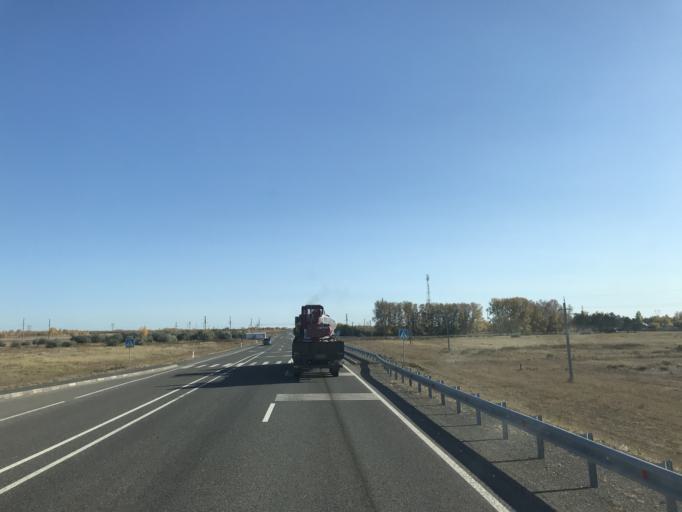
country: KZ
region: Pavlodar
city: Koktobe
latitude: 51.9285
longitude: 77.3315
